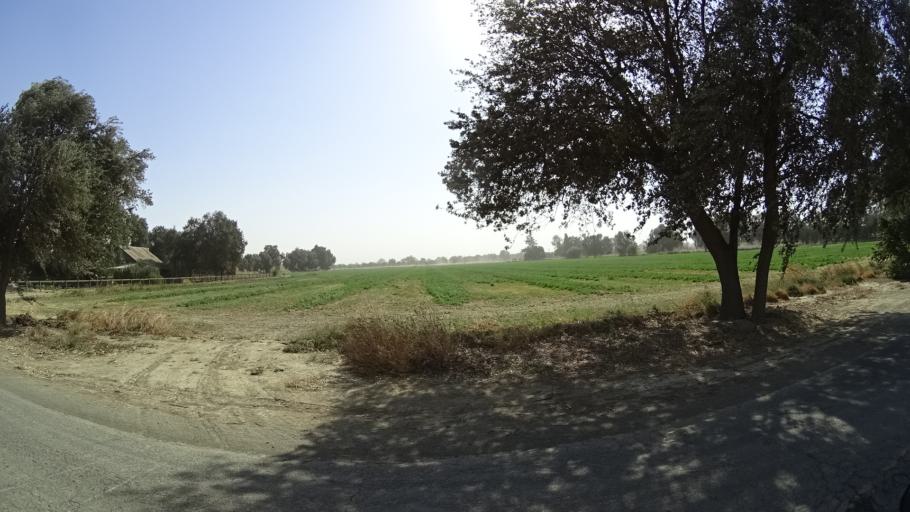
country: US
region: California
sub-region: Yolo County
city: Woodland
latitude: 38.7422
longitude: -121.7850
